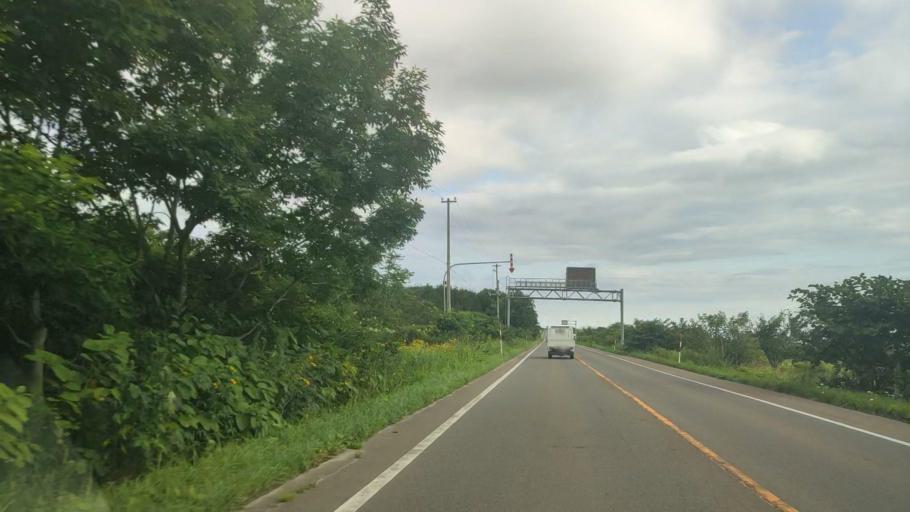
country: JP
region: Hokkaido
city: Niseko Town
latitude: 42.5848
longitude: 140.4511
